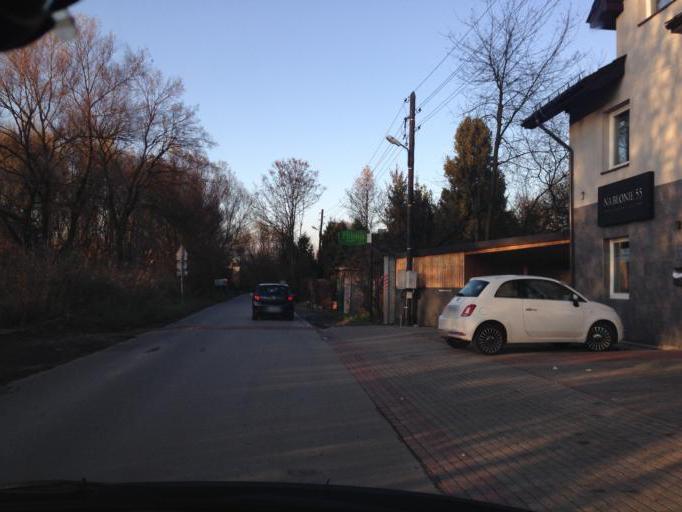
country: PL
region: Lesser Poland Voivodeship
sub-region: Powiat krakowski
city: Rzaska
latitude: 50.0731
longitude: 19.8777
